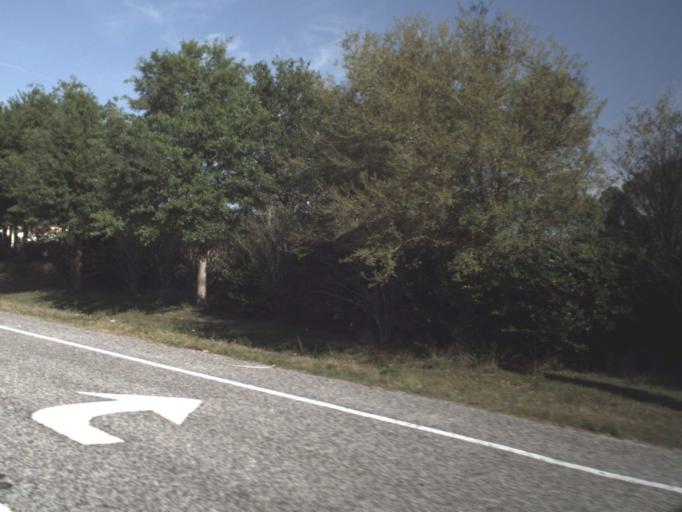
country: US
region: Florida
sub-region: Lake County
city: Minneola
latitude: 28.6394
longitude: -81.7895
